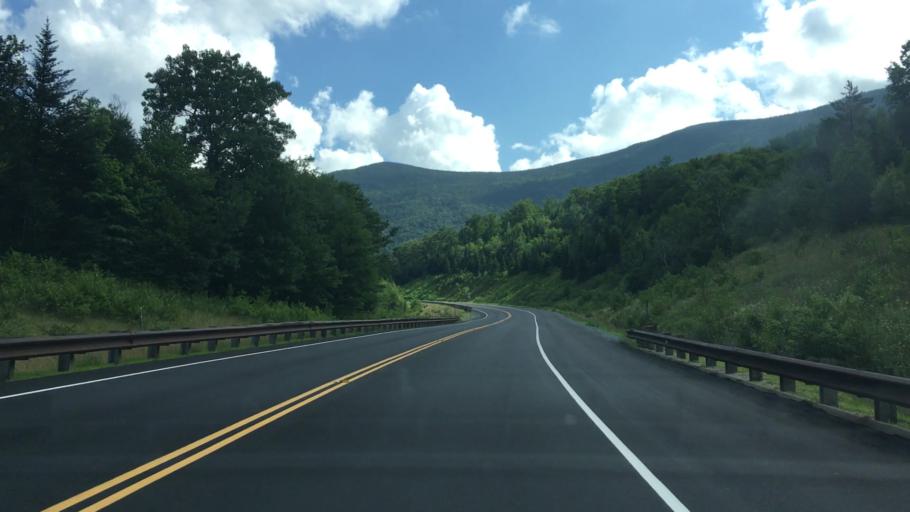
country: US
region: New Hampshire
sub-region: Grafton County
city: Woodstock
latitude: 44.0489
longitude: -71.7929
